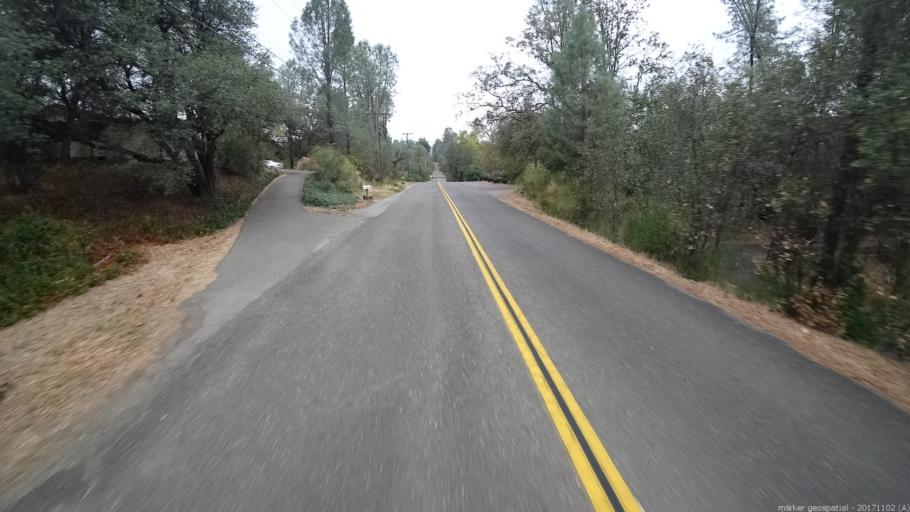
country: US
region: California
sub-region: Shasta County
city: Central Valley (historical)
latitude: 40.6598
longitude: -122.3994
